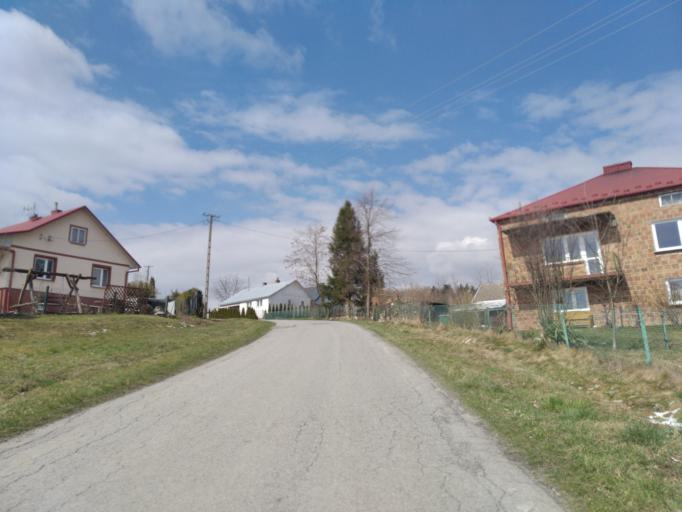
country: PL
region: Subcarpathian Voivodeship
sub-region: Powiat ropczycko-sedziszowski
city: Ropczyce
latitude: 50.0123
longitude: 21.5806
